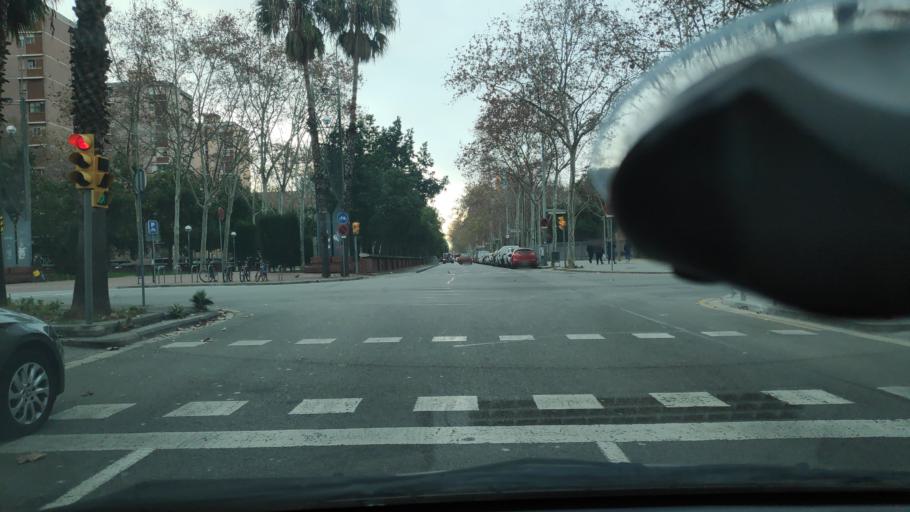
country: ES
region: Catalonia
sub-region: Provincia de Barcelona
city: Sant Marti
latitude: 41.4161
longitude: 2.2127
